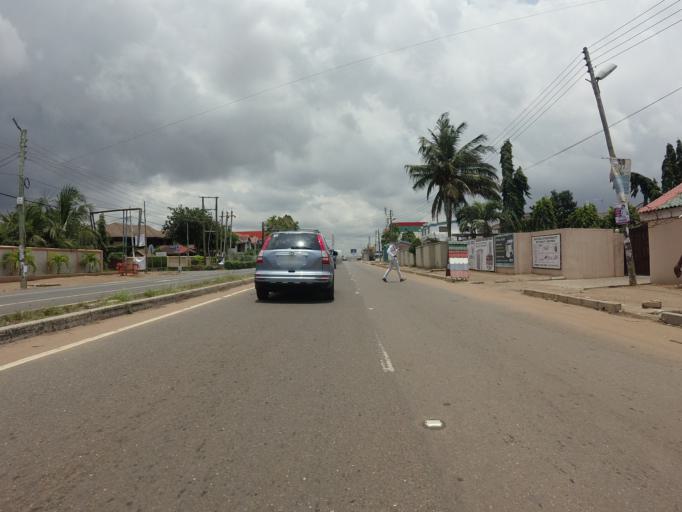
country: GH
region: Greater Accra
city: Medina Estates
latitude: 5.6459
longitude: -0.1492
